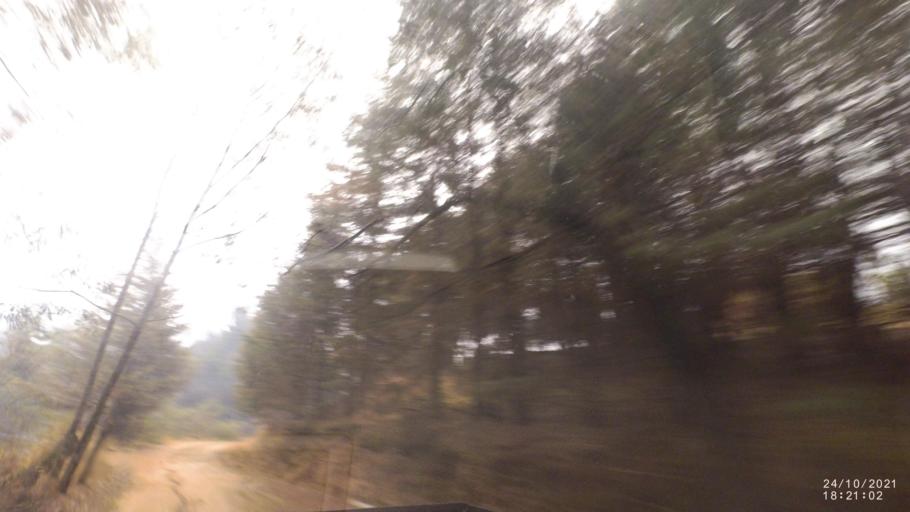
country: BO
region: Cochabamba
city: Cochabamba
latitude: -17.3345
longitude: -66.1403
